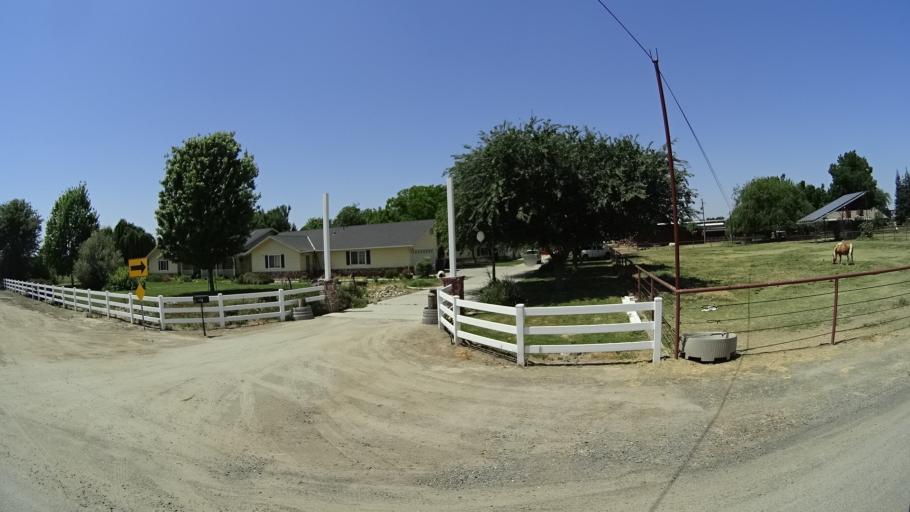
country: US
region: California
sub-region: Kings County
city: Lemoore
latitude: 36.3865
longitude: -119.7632
